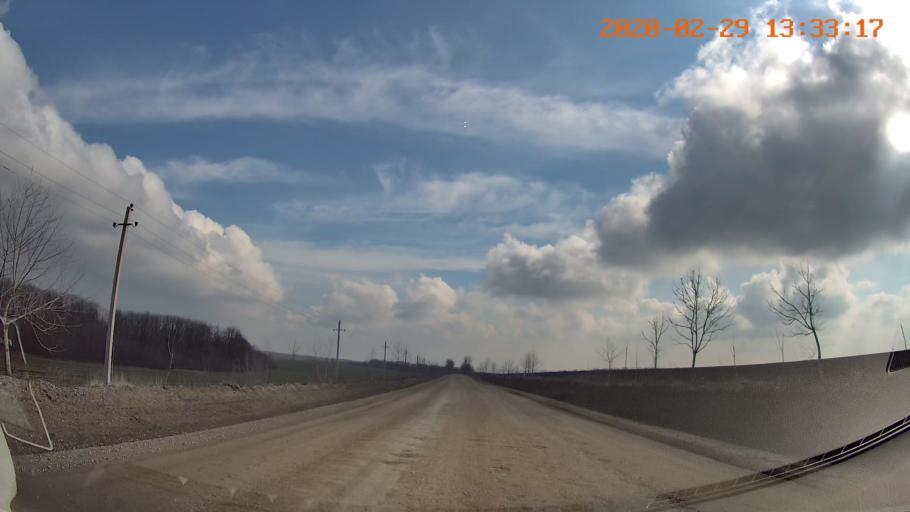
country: MD
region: Telenesti
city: Camenca
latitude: 47.8744
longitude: 28.6153
